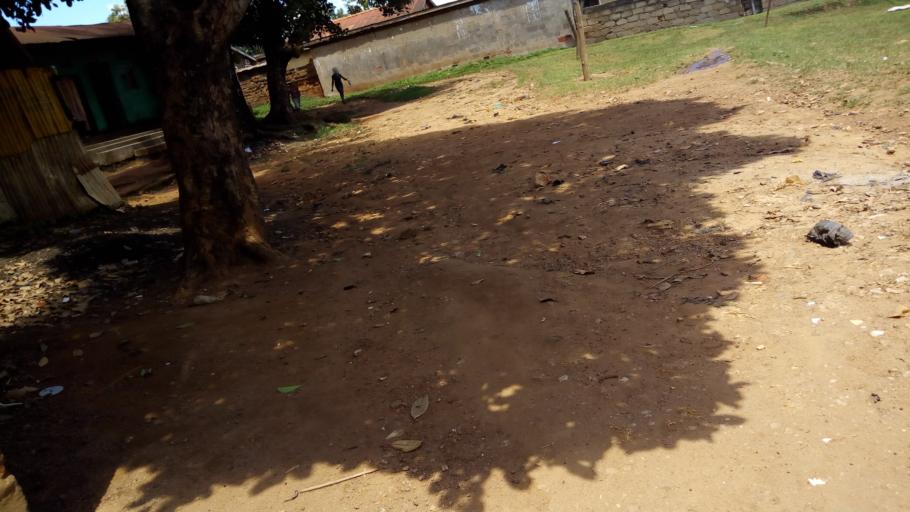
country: UG
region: Central Region
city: Kampala Central Division
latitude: 0.3562
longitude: 32.5580
